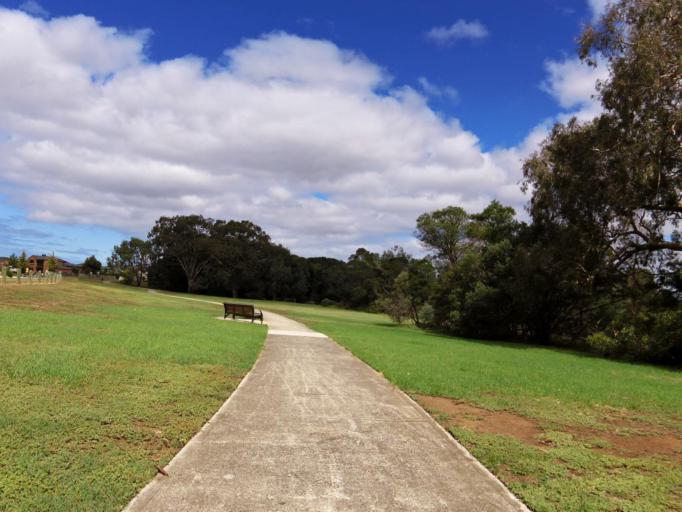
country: AU
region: Victoria
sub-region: Wyndham
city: Tarneit
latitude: -37.8715
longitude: 144.6513
